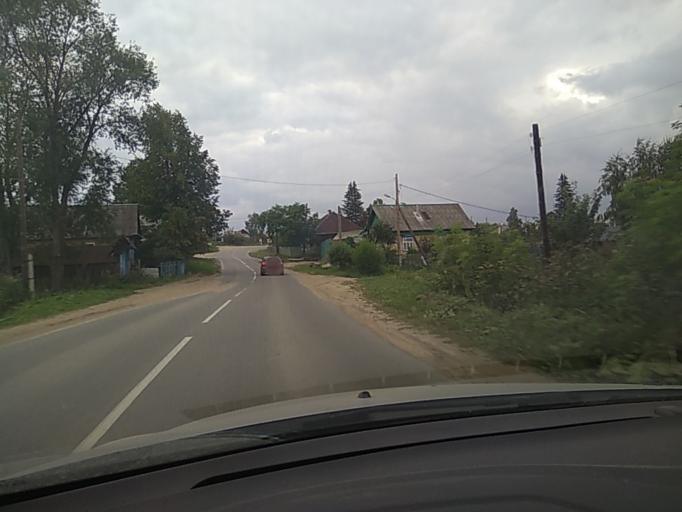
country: RU
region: Chelyabinsk
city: Kyshtym
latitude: 55.7099
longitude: 60.5160
